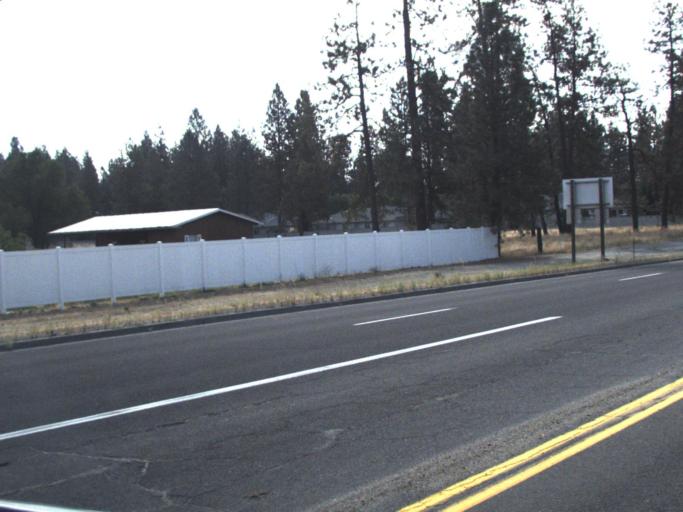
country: US
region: Washington
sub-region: Spokane County
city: Town and Country
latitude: 47.7366
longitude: -117.5075
